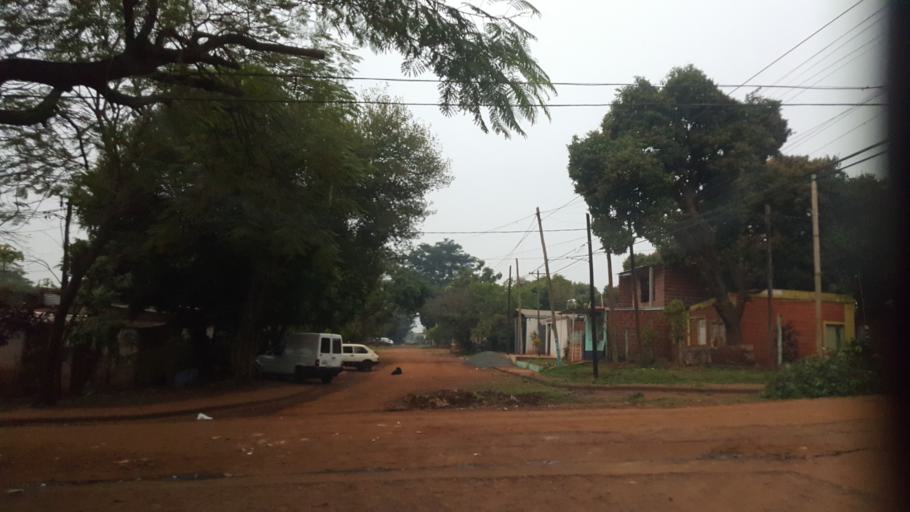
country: AR
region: Misiones
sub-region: Departamento de Capital
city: Posadas
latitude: -27.3970
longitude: -55.9304
